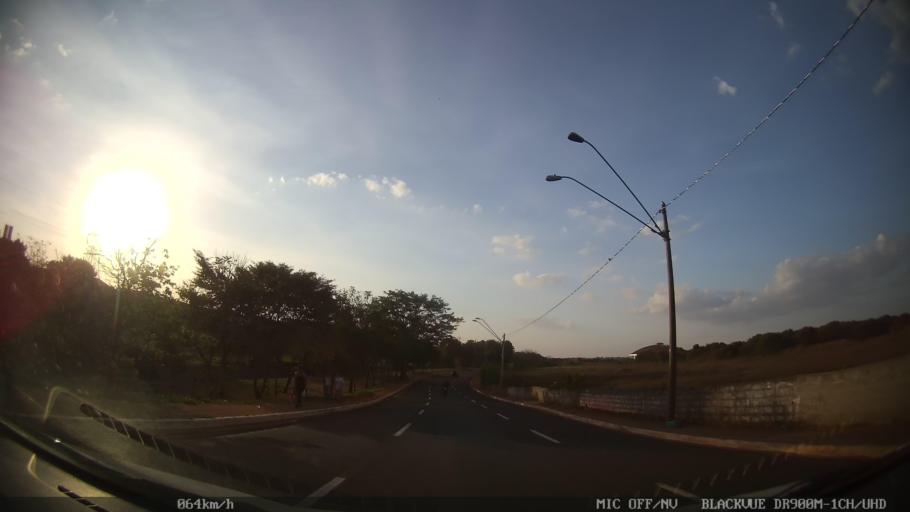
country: BR
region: Sao Paulo
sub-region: Ribeirao Preto
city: Ribeirao Preto
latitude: -21.1362
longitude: -47.8032
